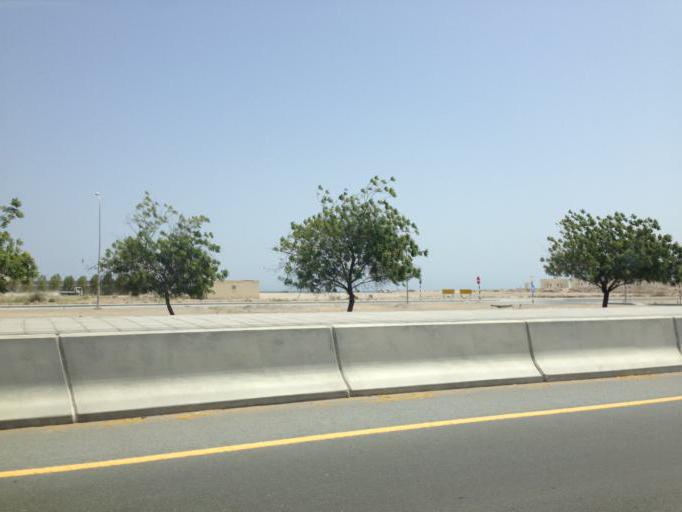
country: OM
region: Muhafazat Masqat
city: Bawshar
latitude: 23.6051
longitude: 58.3246
